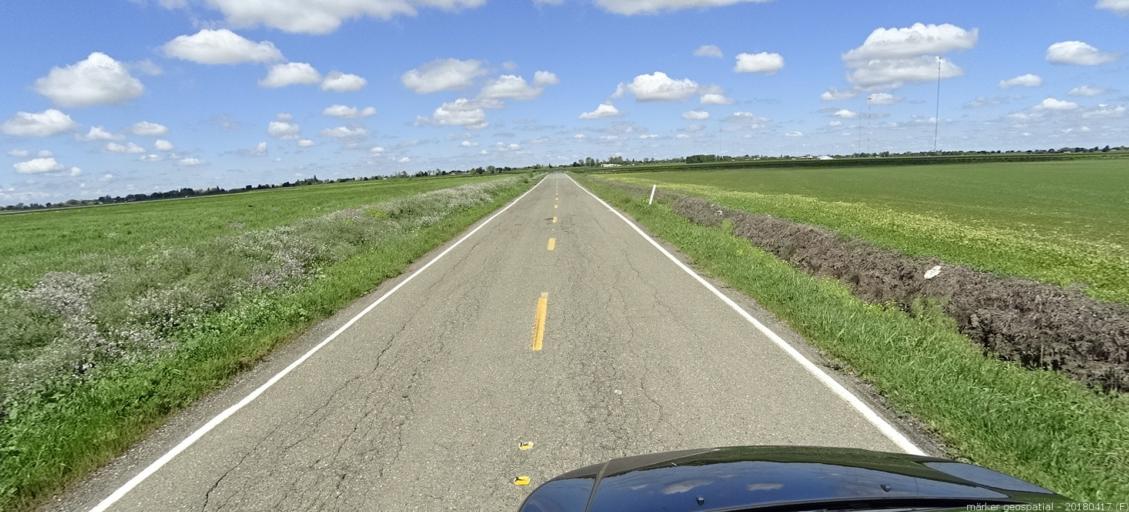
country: US
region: California
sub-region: Sacramento County
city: Walnut Grove
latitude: 38.2101
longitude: -121.5281
